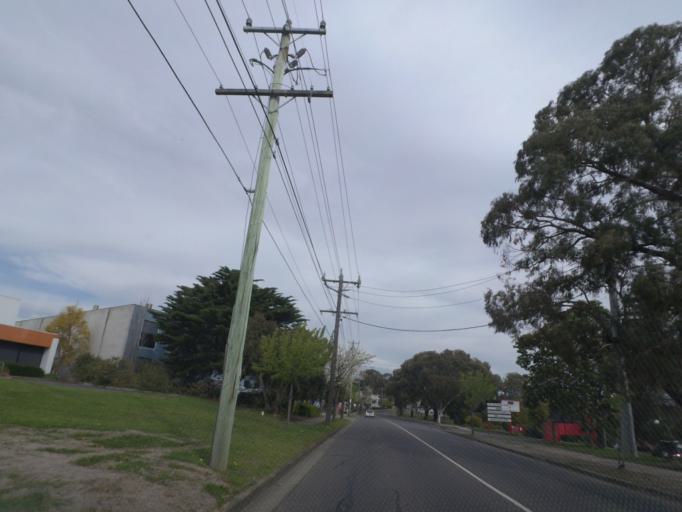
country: AU
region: Victoria
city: Forest Hill
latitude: -37.8339
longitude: 145.1879
